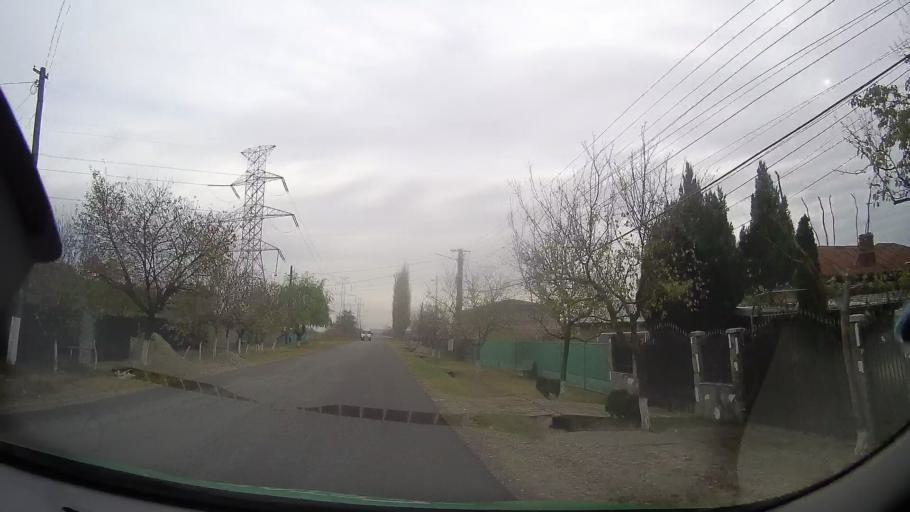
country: RO
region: Prahova
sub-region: Comuna Valea Calugareasca
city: Pantazi
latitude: 44.9299
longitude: 26.1458
